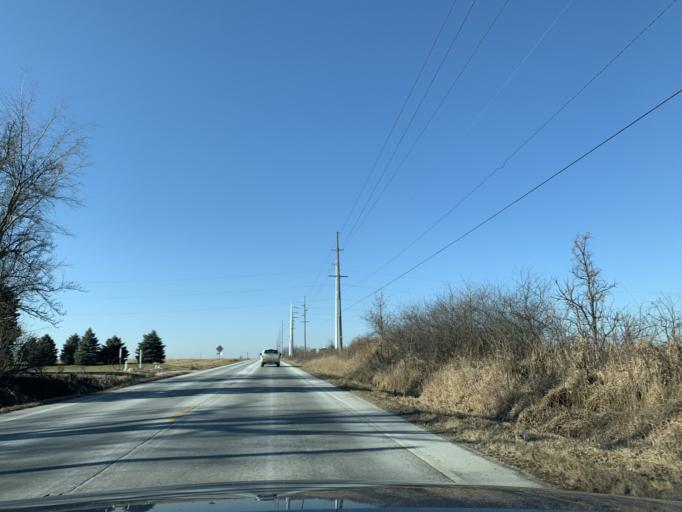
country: US
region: Indiana
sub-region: Lake County
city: Saint John
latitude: 41.4209
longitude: -87.4217
